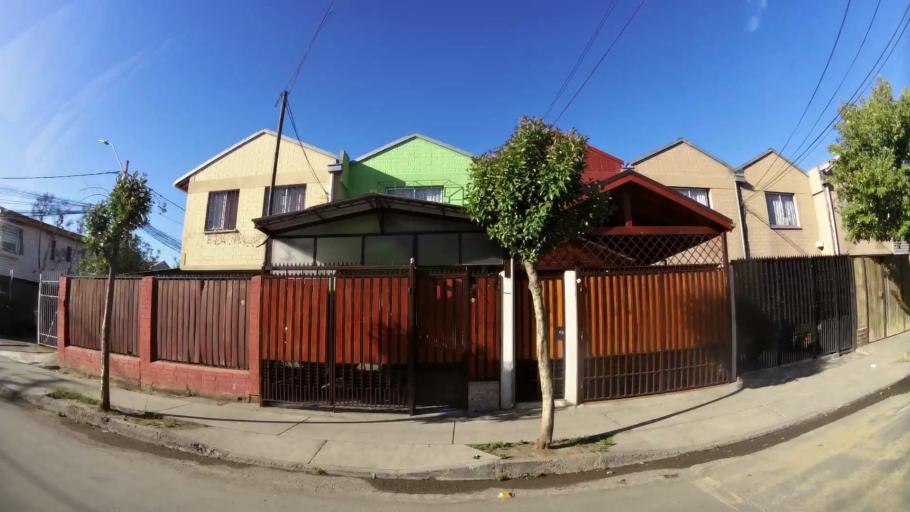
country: CL
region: Santiago Metropolitan
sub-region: Provincia de Maipo
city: San Bernardo
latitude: -33.6006
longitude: -70.6807
